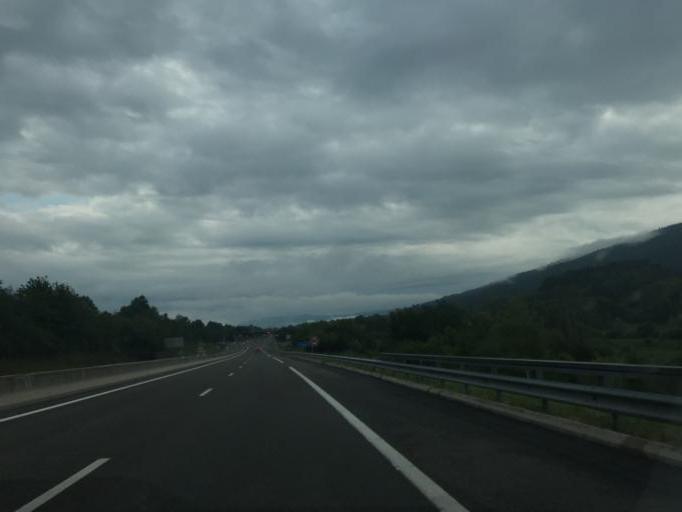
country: FR
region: Rhone-Alpes
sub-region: Departement de l'Ain
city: Groissiat
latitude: 46.2194
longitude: 5.6104
